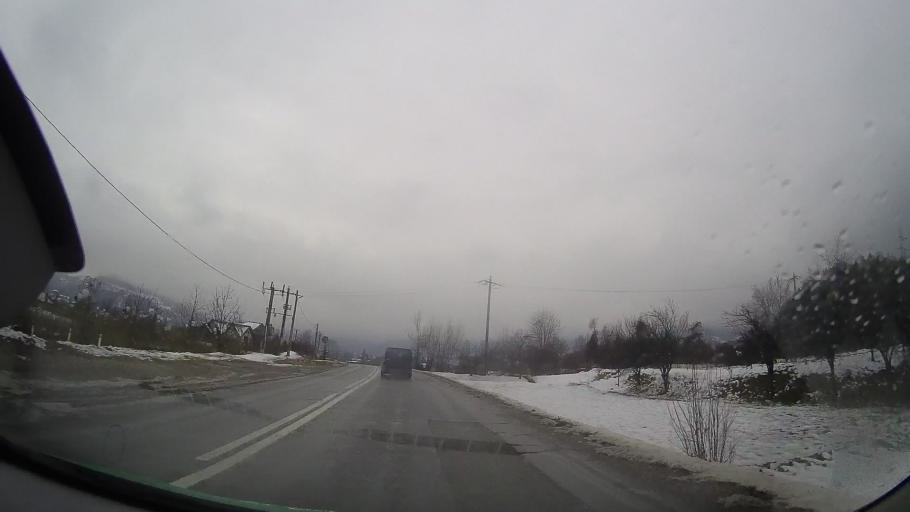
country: RO
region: Neamt
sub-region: Comuna Pangarati
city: Stejaru
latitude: 46.9241
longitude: 26.1906
